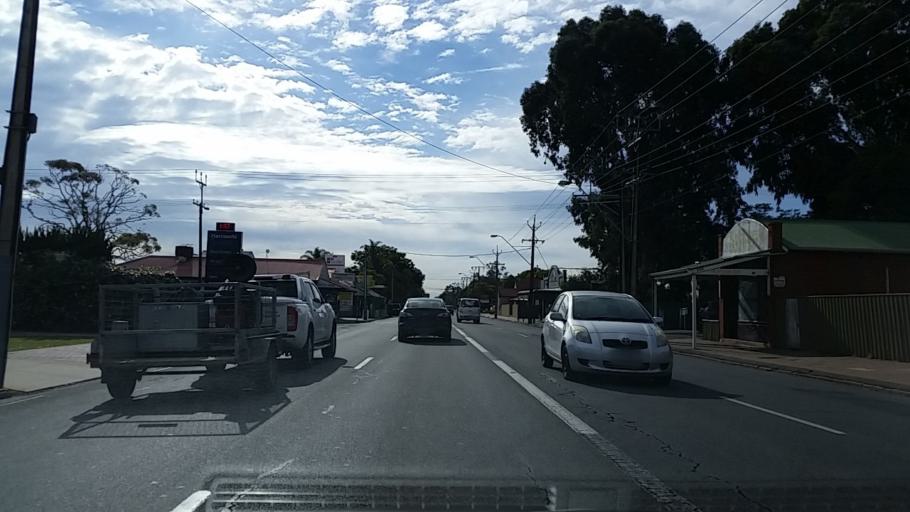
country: AU
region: South Australia
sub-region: Mitcham
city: Clarence Gardens
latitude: -34.9715
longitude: 138.5912
